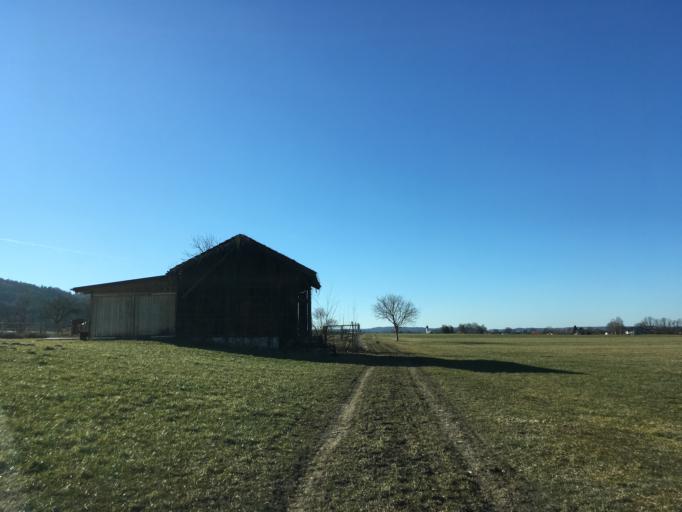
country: DE
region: Bavaria
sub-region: Upper Bavaria
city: Bruckmuhl
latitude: 47.8655
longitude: 11.9107
